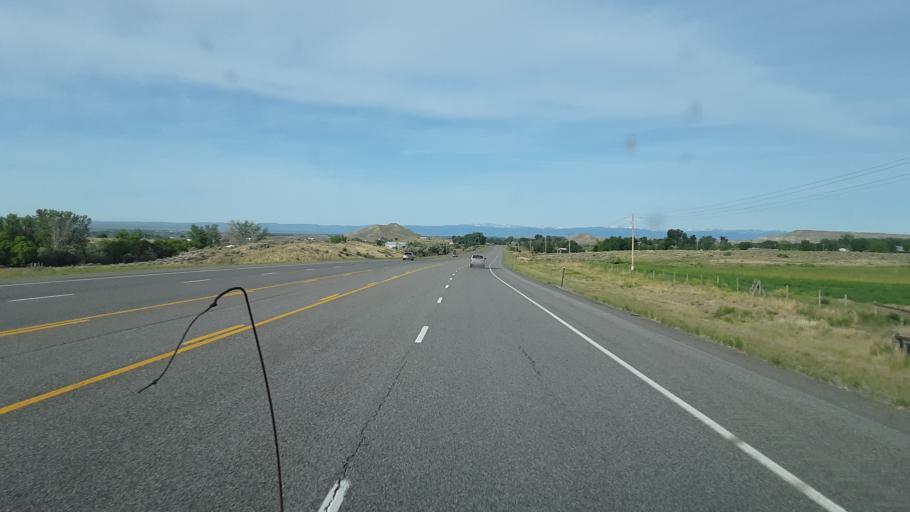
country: US
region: Wyoming
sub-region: Fremont County
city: Riverton
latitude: 43.1385
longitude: -108.2952
